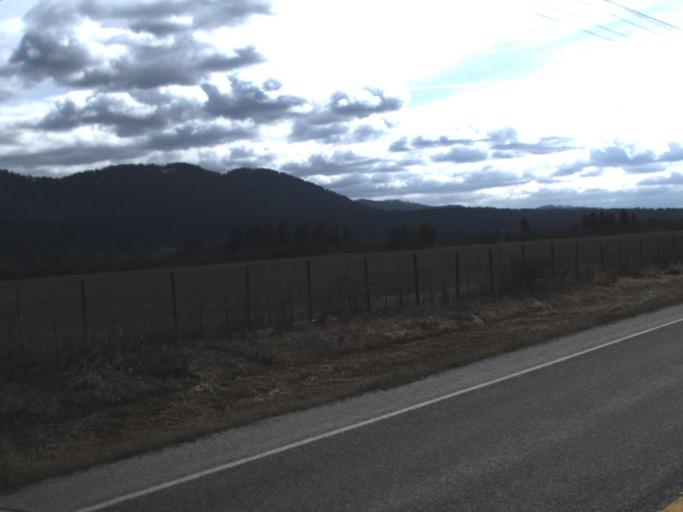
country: US
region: Washington
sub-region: Pend Oreille County
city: Newport
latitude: 48.3800
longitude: -117.3078
